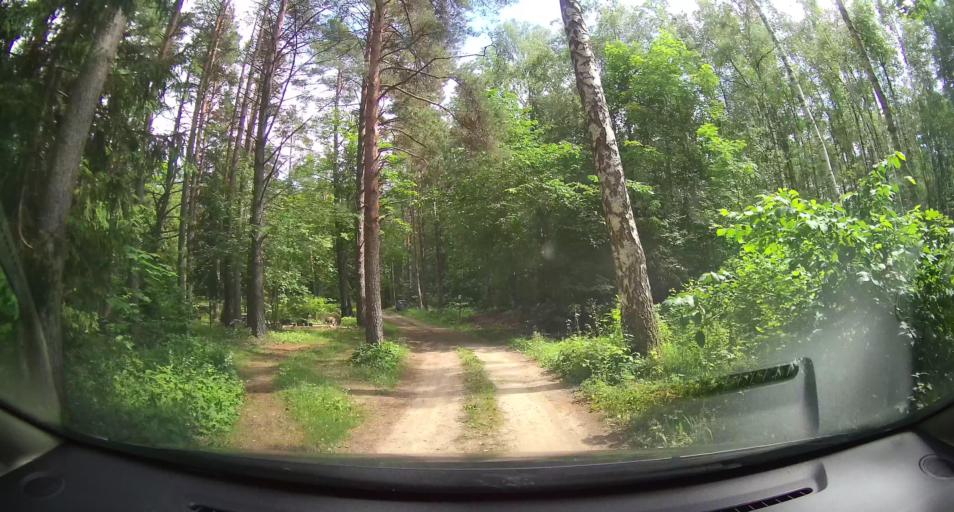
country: EE
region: Laeaene
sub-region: Lihula vald
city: Lihula
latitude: 58.6394
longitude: 23.6969
